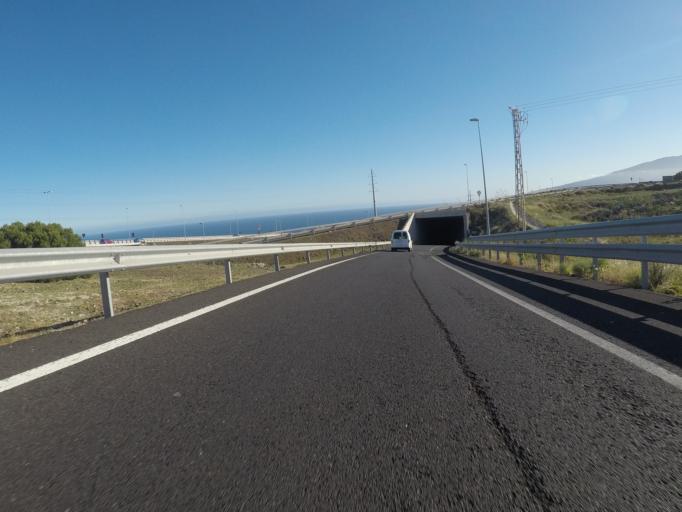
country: ES
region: Canary Islands
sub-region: Provincia de Santa Cruz de Tenerife
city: La Laguna
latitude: 28.4175
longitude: -16.3119
